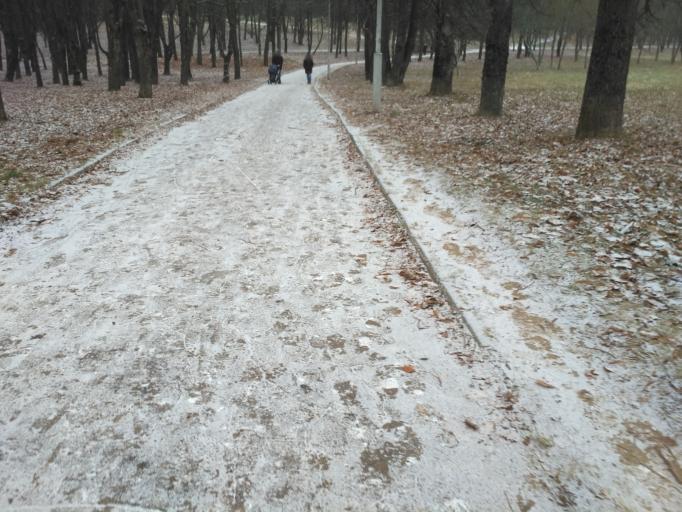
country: BY
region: Minsk
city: Novoye Medvezhino
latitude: 53.9183
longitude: 27.4838
